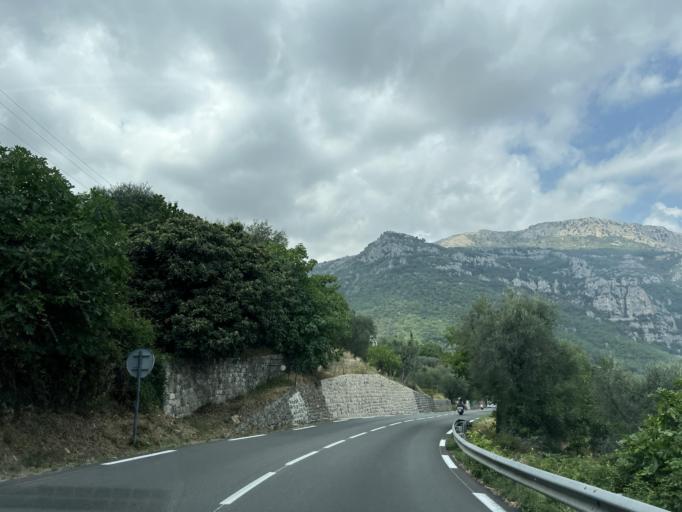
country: FR
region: Provence-Alpes-Cote d'Azur
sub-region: Departement des Alpes-Maritimes
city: Le Rouret
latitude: 43.7064
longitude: 6.9908
